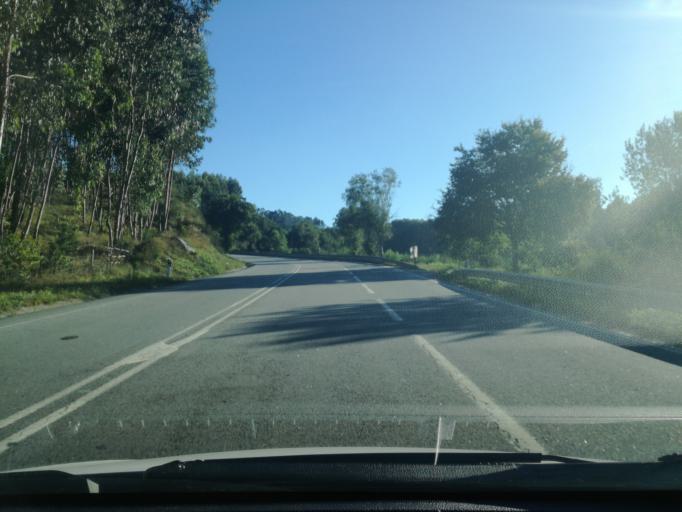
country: PT
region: Braga
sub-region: Vieira do Minho
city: Real
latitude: 41.6176
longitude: -8.2311
